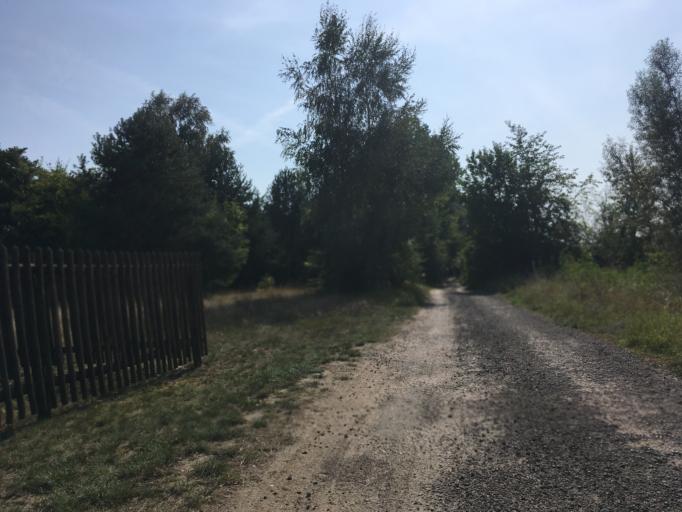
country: DE
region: Brandenburg
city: Erkner
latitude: 52.4041
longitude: 13.7307
